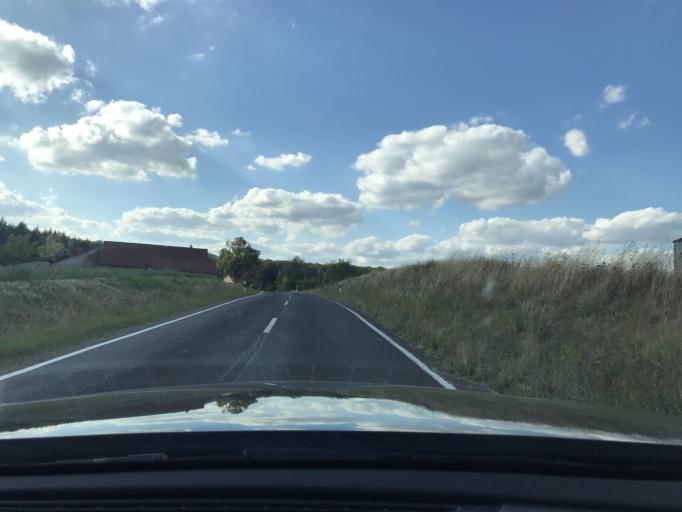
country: DE
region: Bavaria
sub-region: Regierungsbezirk Unterfranken
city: Kirchlauter
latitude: 50.0754
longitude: 10.6626
